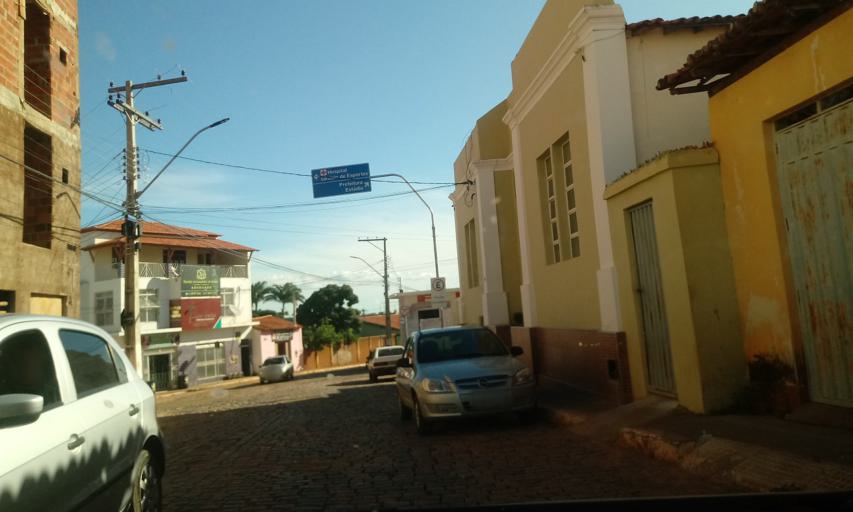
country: BR
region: Bahia
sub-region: Riacho De Santana
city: Riacho de Santana
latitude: -13.7716
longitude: -42.7140
